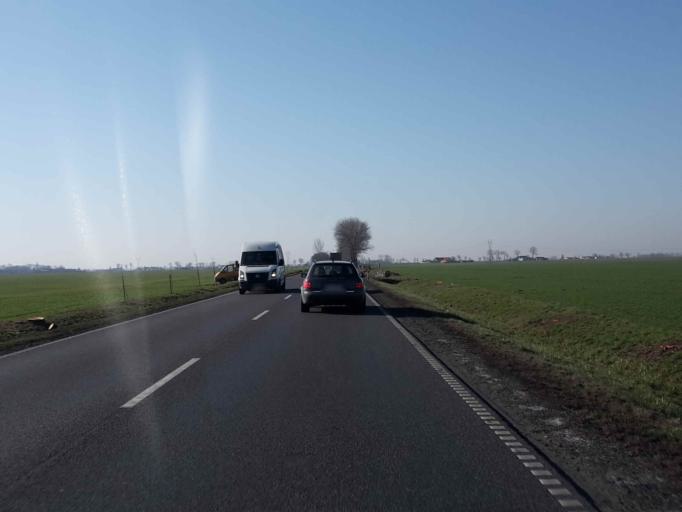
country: PL
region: Kujawsko-Pomorskie
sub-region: Powiat mogilenski
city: Strzelno
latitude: 52.6938
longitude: 18.2093
